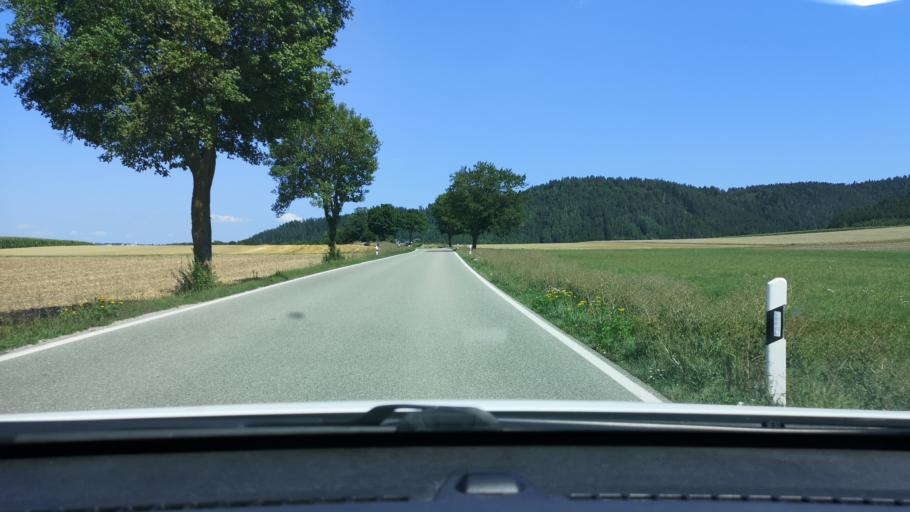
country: DE
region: Baden-Wuerttemberg
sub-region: Freiburg Region
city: Muhlheim am Bach
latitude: 48.3606
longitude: 8.6961
